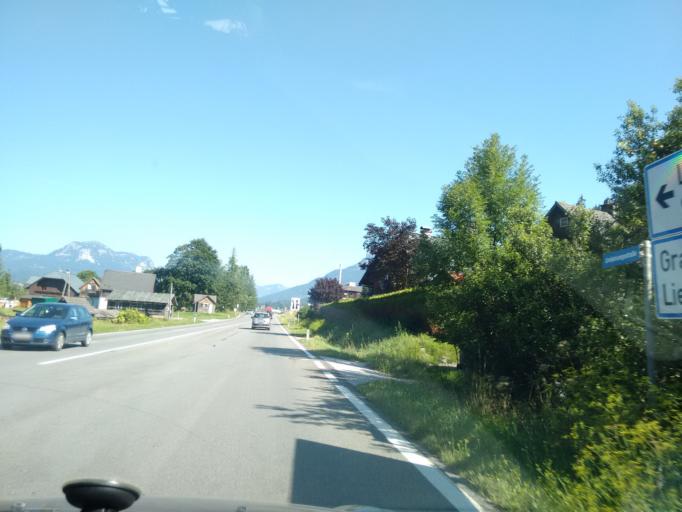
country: AT
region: Styria
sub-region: Politischer Bezirk Liezen
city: Bad Aussee
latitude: 47.5936
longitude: 13.7938
